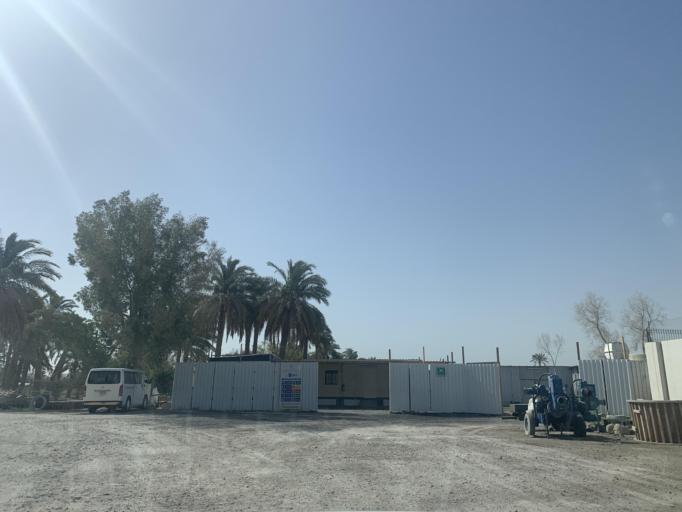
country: BH
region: Manama
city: Jidd Hafs
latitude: 26.2080
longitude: 50.5591
